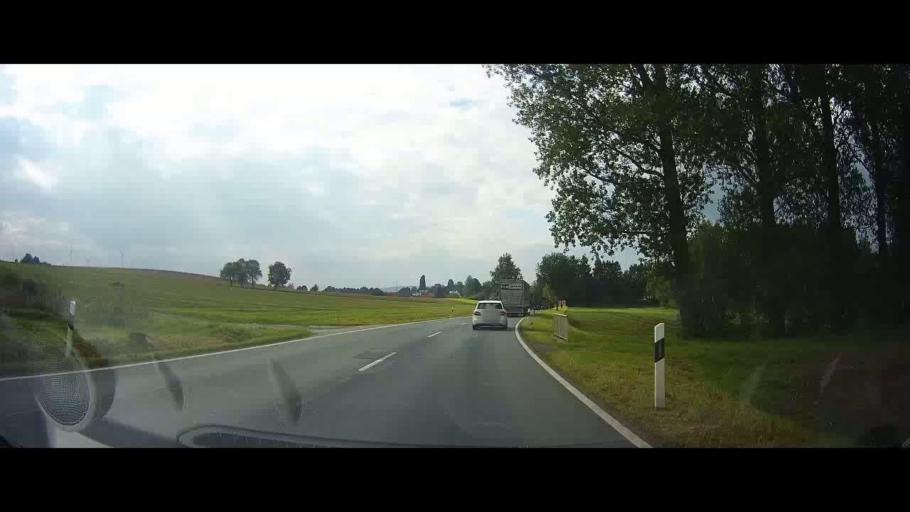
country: DE
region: Lower Saxony
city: Uslar
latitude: 51.6529
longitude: 9.6863
